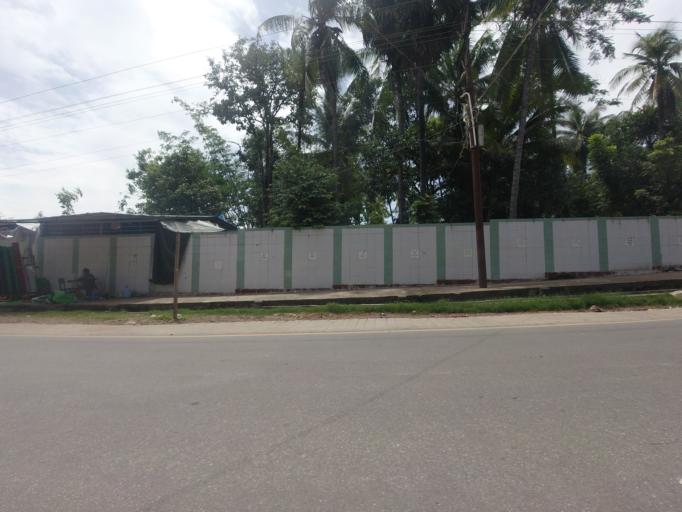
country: MM
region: Mon
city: Mawlamyine
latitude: 16.4521
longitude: 97.6338
